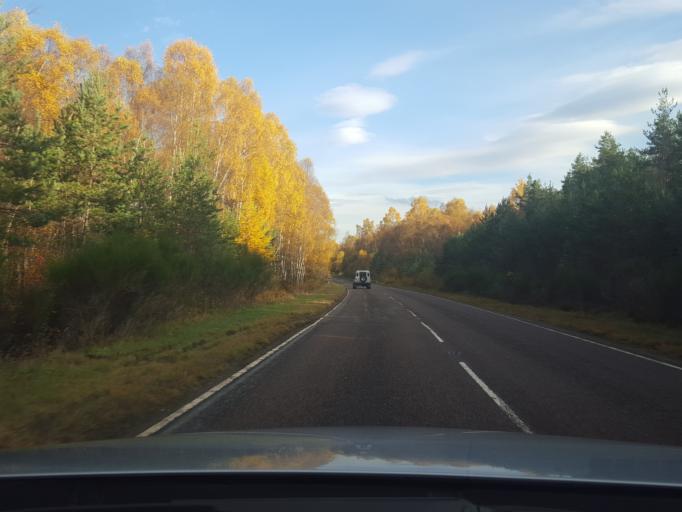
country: GB
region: Scotland
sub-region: Highland
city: Spean Bridge
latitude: 57.1704
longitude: -4.8146
